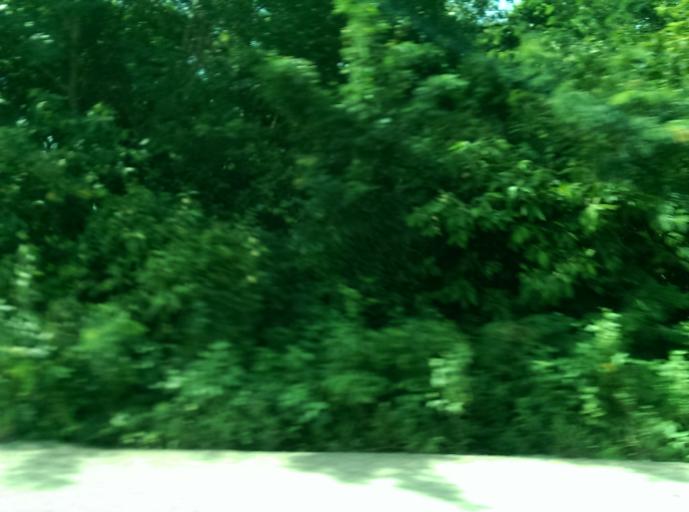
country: MX
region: Quintana Roo
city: Tulum
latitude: 20.2231
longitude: -87.4566
